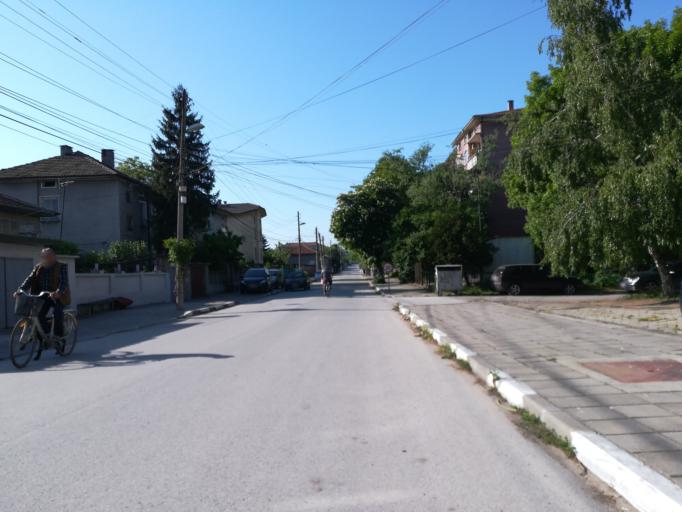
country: BG
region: Stara Zagora
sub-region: Obshtina Chirpan
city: Chirpan
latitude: 42.1052
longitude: 25.2247
